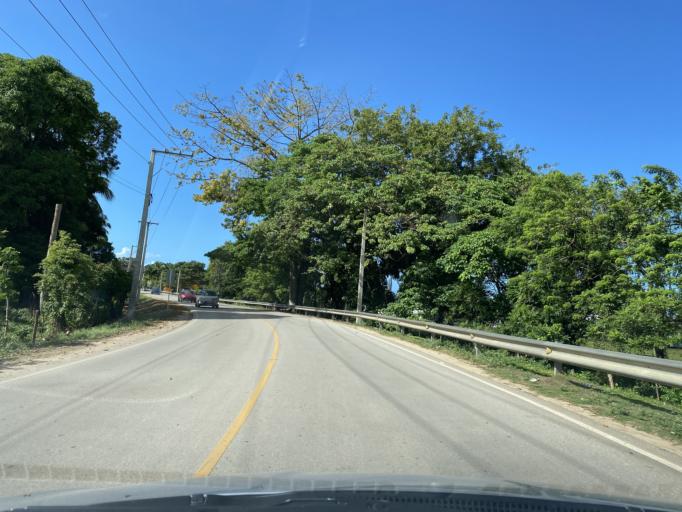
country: DO
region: Samana
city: Las Terrenas
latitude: 19.3063
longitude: -69.5506
